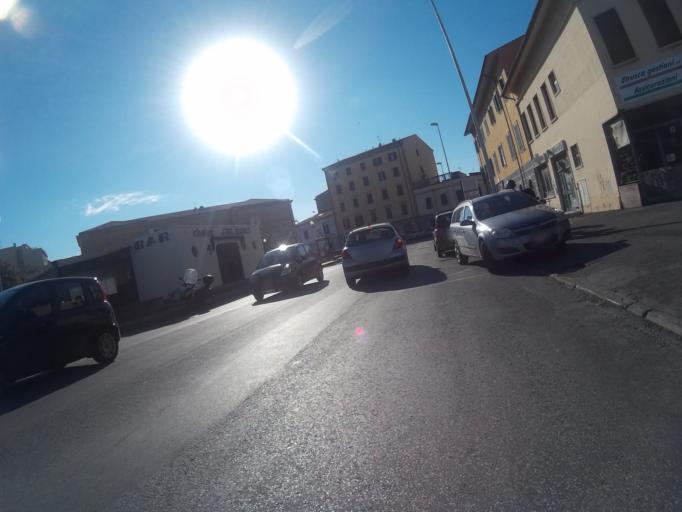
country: IT
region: Tuscany
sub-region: Provincia di Livorno
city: Livorno
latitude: 43.5602
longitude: 10.3149
